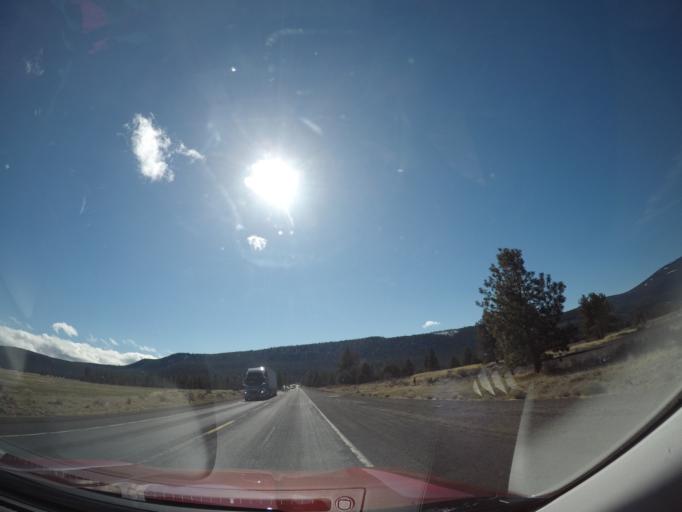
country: US
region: California
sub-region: Siskiyou County
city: Montague
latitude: 41.7653
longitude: -122.0590
